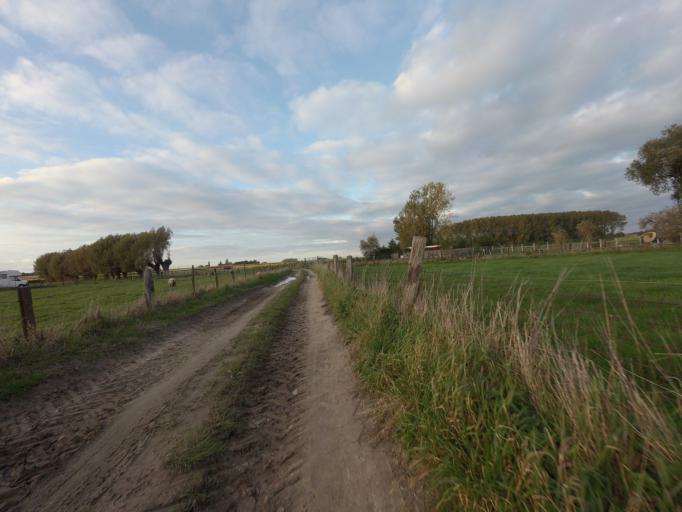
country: BE
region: Flanders
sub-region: Provincie Vlaams-Brabant
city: Grimbergen
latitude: 50.9401
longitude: 4.3534
